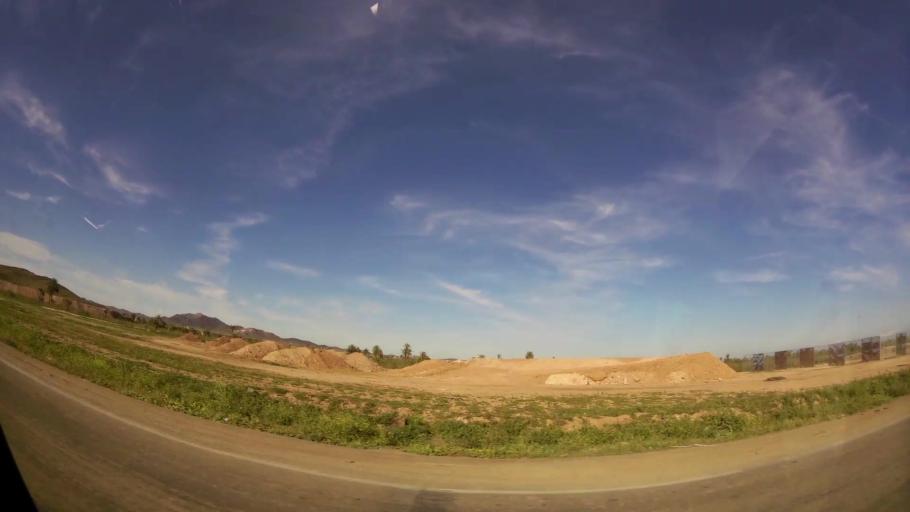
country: MA
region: Marrakech-Tensift-Al Haouz
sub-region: Marrakech
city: Marrakesh
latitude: 31.6968
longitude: -8.0587
